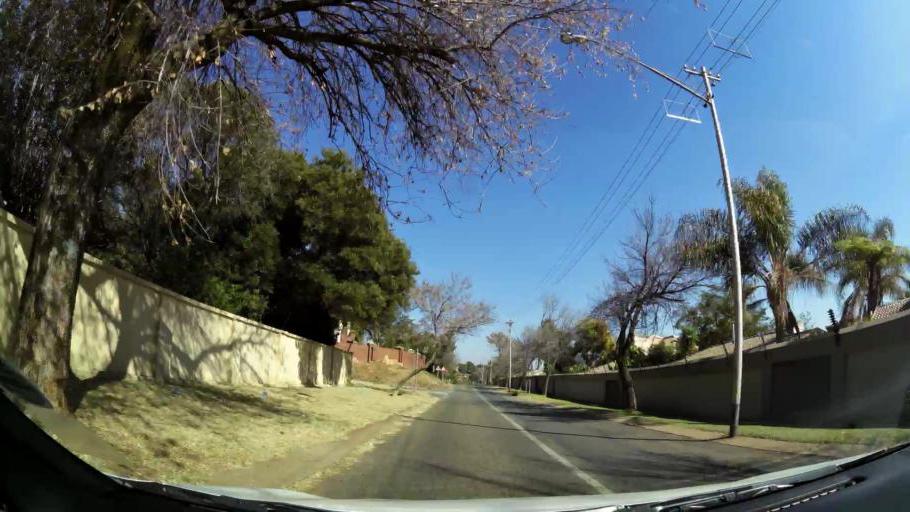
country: ZA
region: Gauteng
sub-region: City of Tshwane Metropolitan Municipality
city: Pretoria
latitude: -25.7988
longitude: 28.2274
